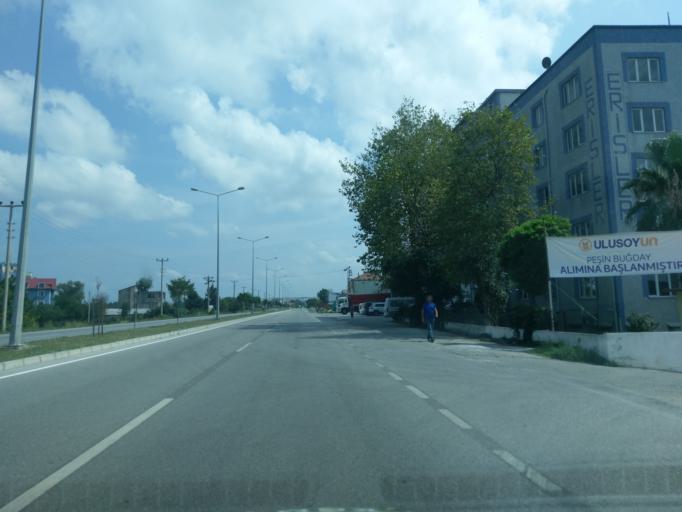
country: TR
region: Samsun
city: Bafra
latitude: 41.5736
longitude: 35.8654
